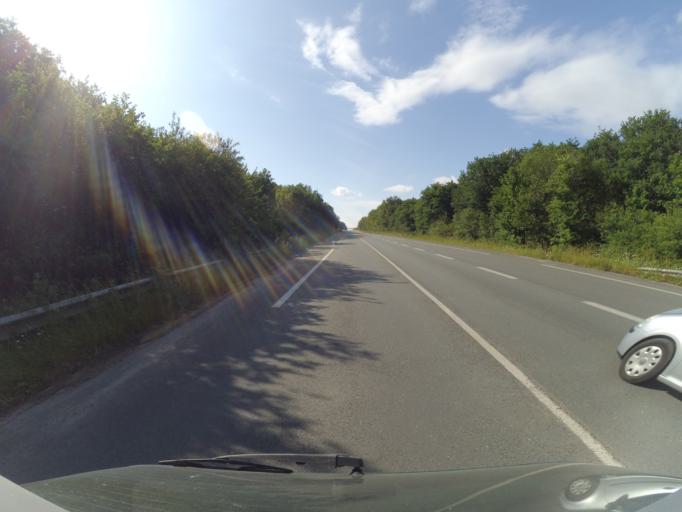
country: FR
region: Poitou-Charentes
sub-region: Departement de la Charente-Maritime
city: Saint-Agnant
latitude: 45.8362
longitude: -0.9414
